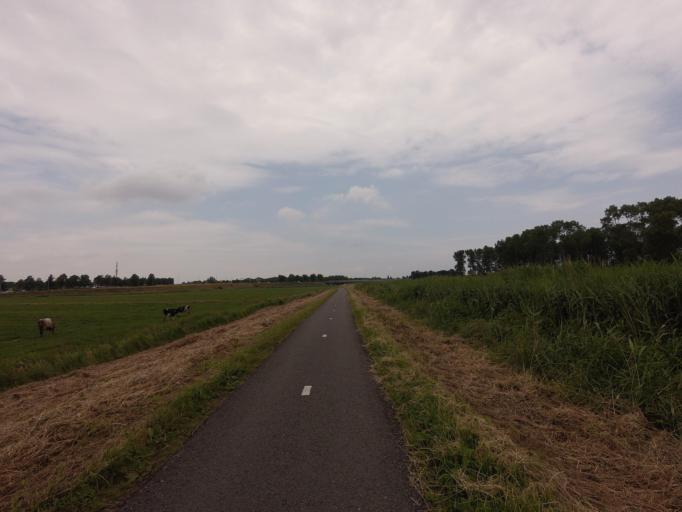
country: NL
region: North Holland
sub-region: Gemeente Purmerend
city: Purmerend
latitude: 52.4831
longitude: 4.9537
